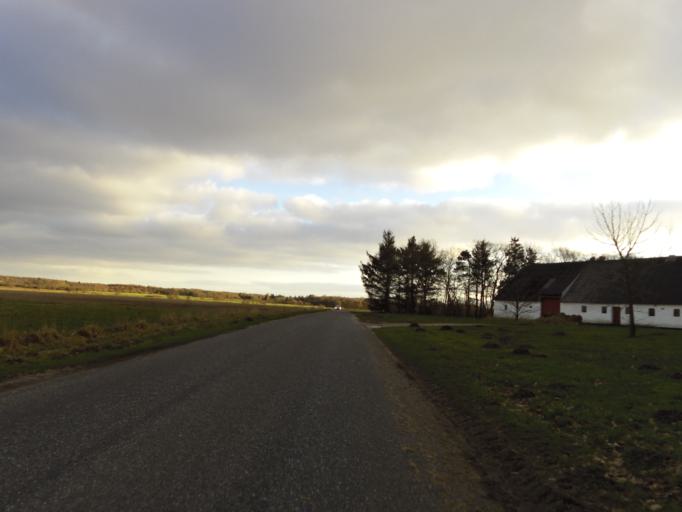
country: DK
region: South Denmark
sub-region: Esbjerg Kommune
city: Ribe
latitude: 55.2993
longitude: 8.8500
